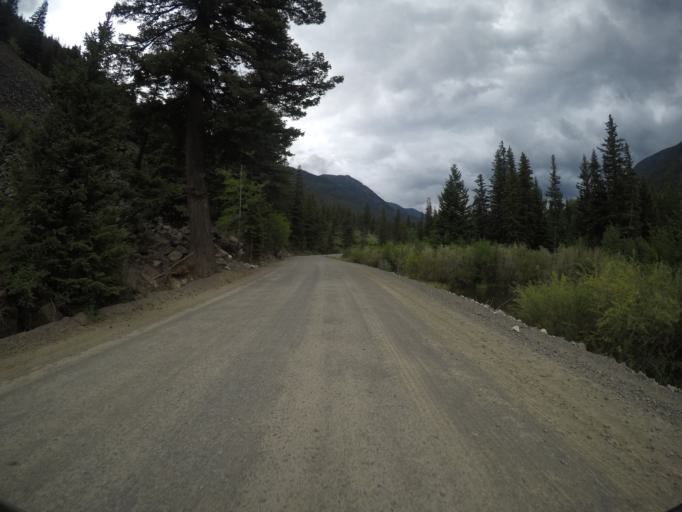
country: US
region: Montana
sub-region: Park County
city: Livingston
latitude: 45.4728
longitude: -110.2008
